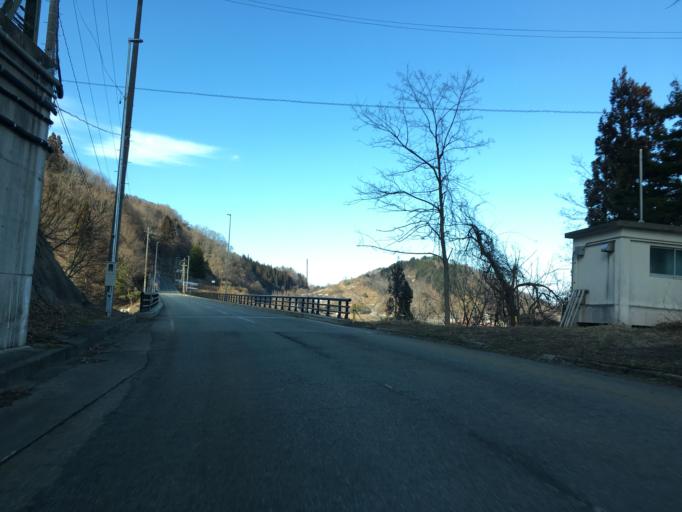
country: JP
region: Yamagata
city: Nagai
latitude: 37.9691
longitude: 139.9153
